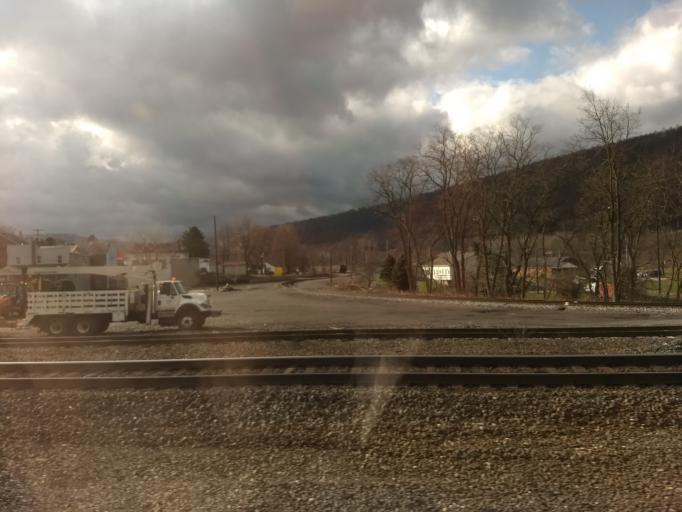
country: US
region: Pennsylvania
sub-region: Cambria County
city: Salix
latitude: 40.3662
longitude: -78.7943
